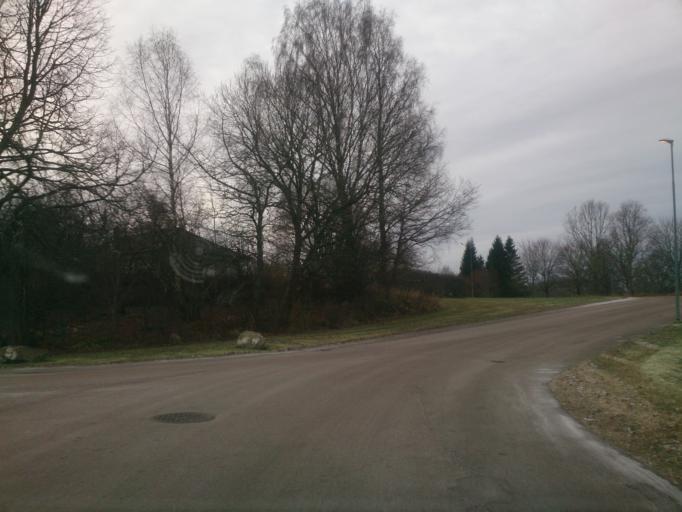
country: SE
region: OEstergoetland
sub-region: Atvidabergs Kommun
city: Atvidaberg
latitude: 58.2028
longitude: 15.9722
